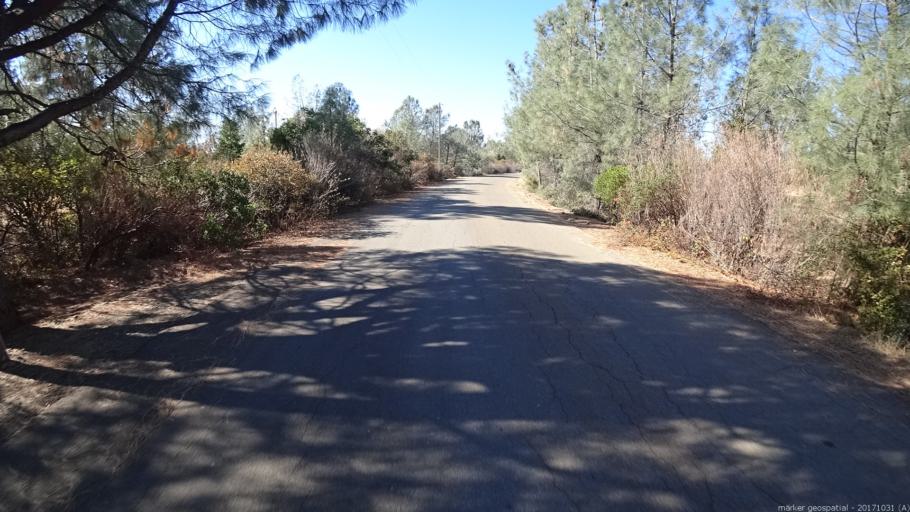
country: US
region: California
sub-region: Shasta County
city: Shingletown
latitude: 40.5083
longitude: -122.0228
